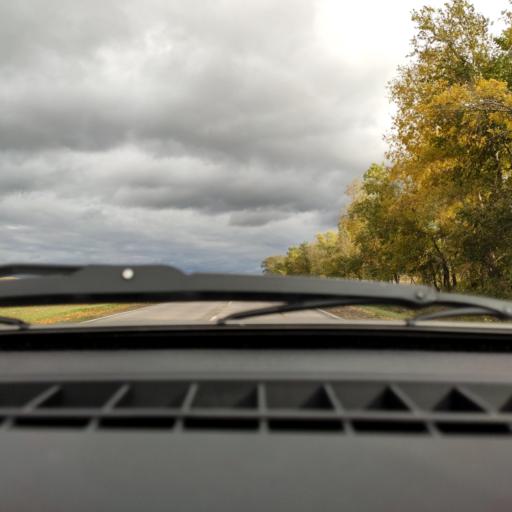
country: RU
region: Bashkortostan
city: Shafranovo
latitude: 54.0138
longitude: 54.8511
